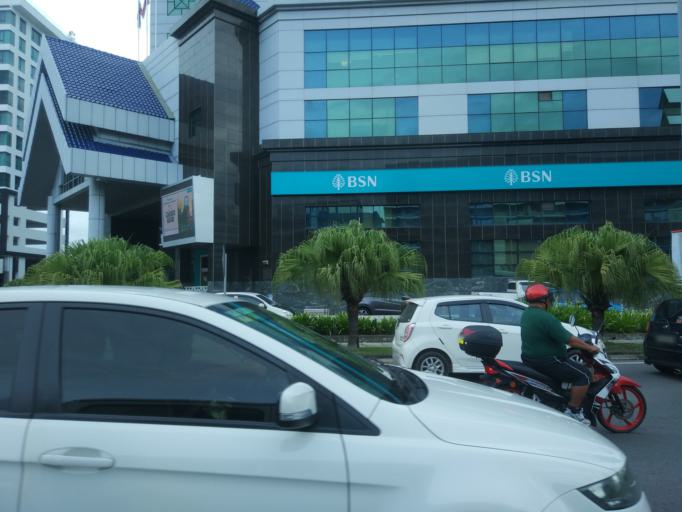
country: MY
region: Sabah
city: Kota Kinabalu
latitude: 5.9714
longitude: 116.0707
